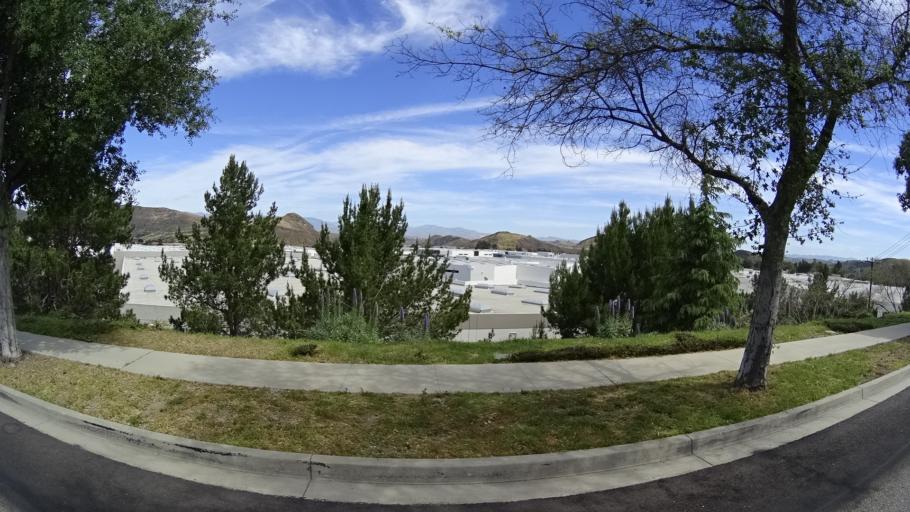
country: US
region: California
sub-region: Ventura County
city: Casa Conejo
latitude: 34.1992
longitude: -118.9310
